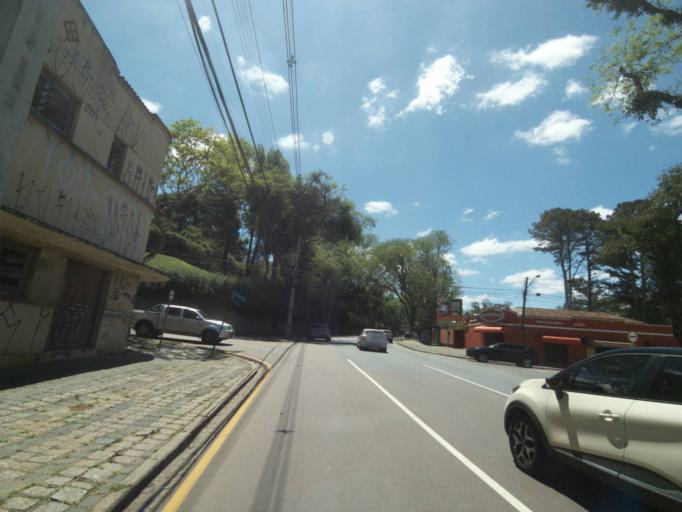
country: BR
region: Parana
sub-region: Curitiba
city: Curitiba
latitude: -25.3978
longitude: -49.2715
